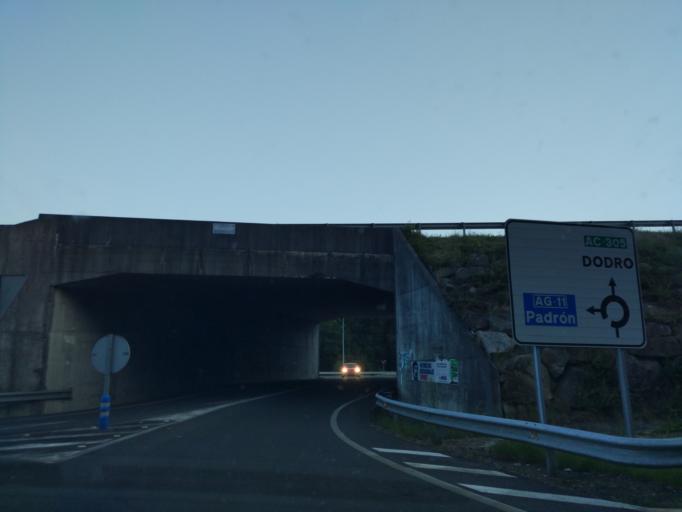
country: ES
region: Galicia
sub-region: Provincia da Coruna
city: Padron
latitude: 42.7265
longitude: -8.6752
